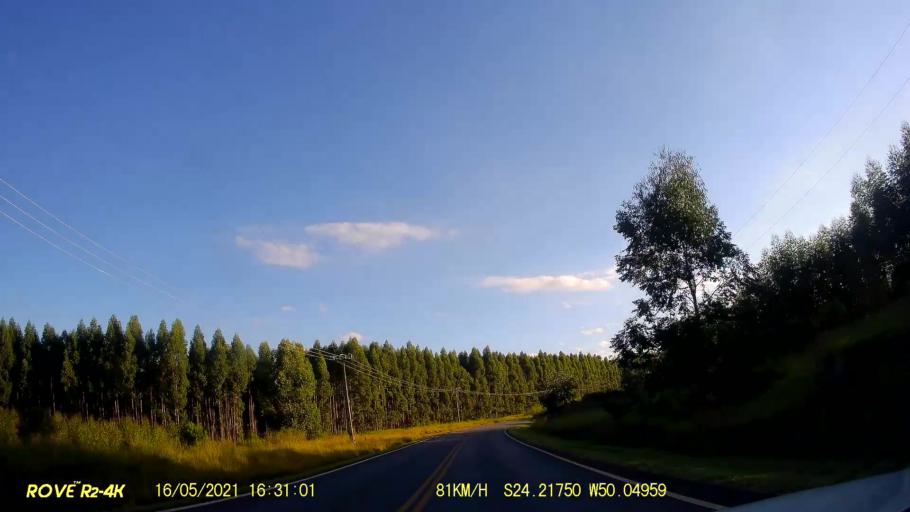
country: BR
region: Parana
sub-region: Pirai Do Sul
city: Pirai do Sul
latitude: -24.2177
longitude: -50.0498
